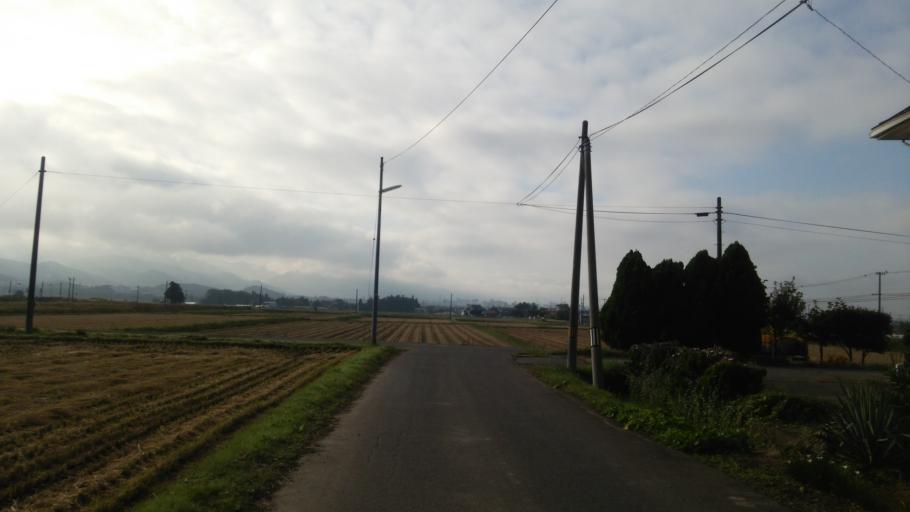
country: JP
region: Fukushima
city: Kitakata
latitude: 37.5428
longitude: 139.9295
